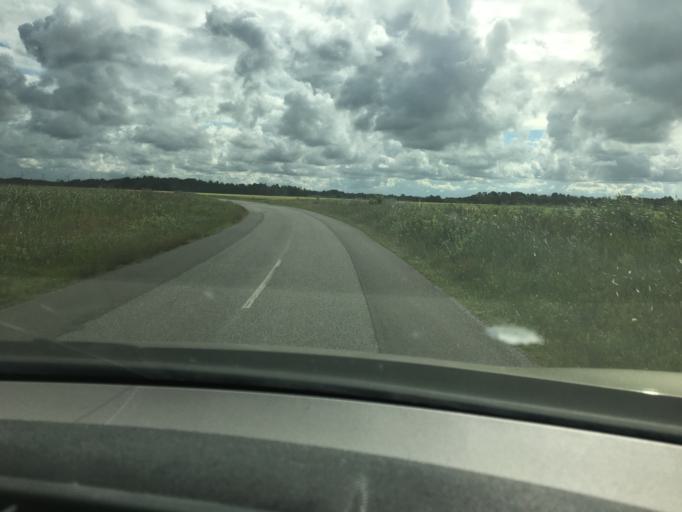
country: DK
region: South Denmark
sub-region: Varde Kommune
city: Oksbol
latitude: 55.8315
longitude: 8.2517
